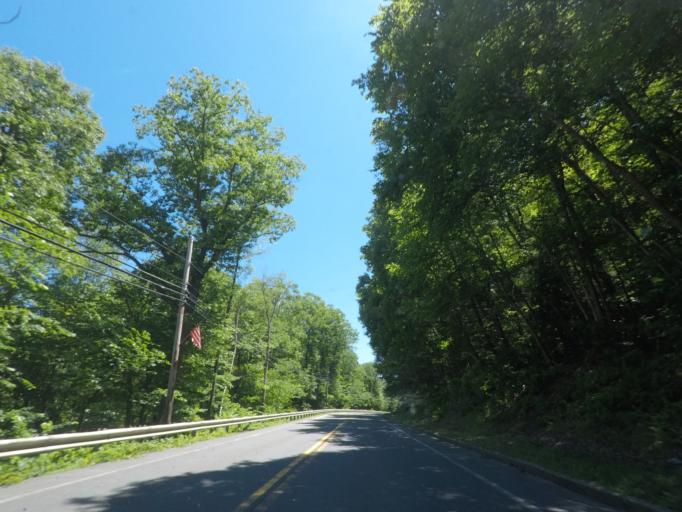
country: US
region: Massachusetts
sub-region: Berkshire County
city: Becket
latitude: 42.2743
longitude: -72.9707
